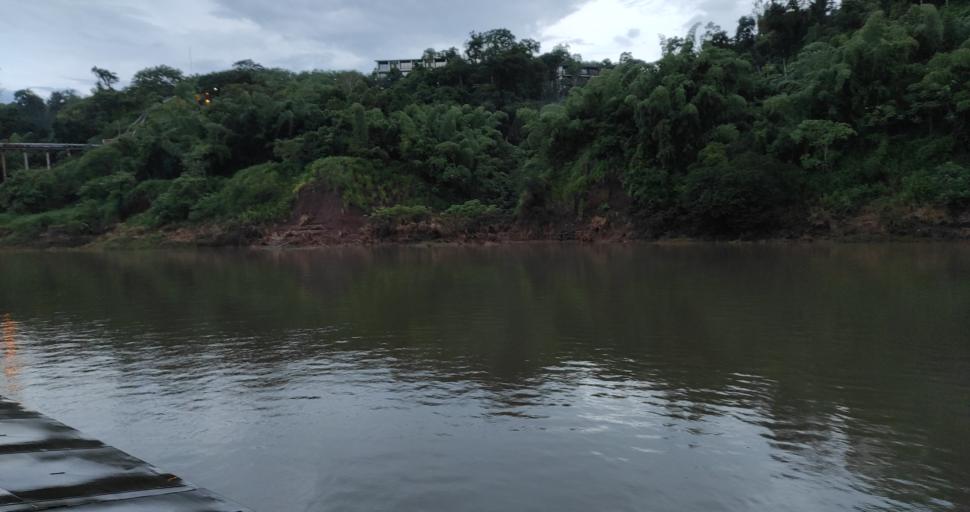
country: AR
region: Misiones
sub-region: Departamento de Iguazu
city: Puerto Iguazu
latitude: -25.5912
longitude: -54.5669
